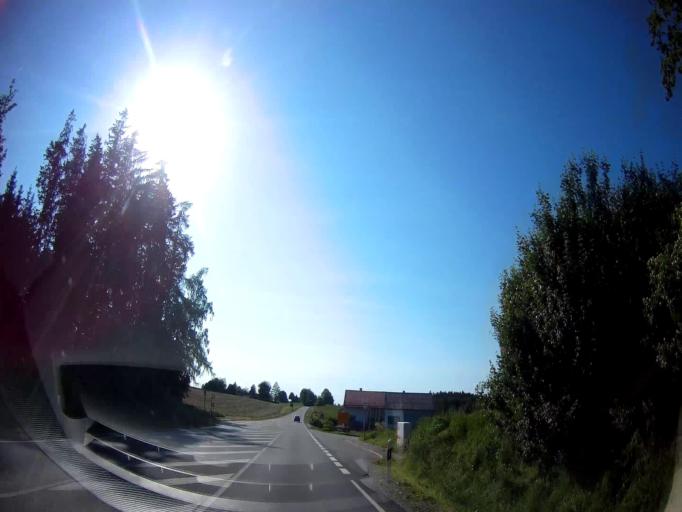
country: DE
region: Bavaria
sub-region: Lower Bavaria
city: Wurmannsquick
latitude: 48.3480
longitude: 12.8081
